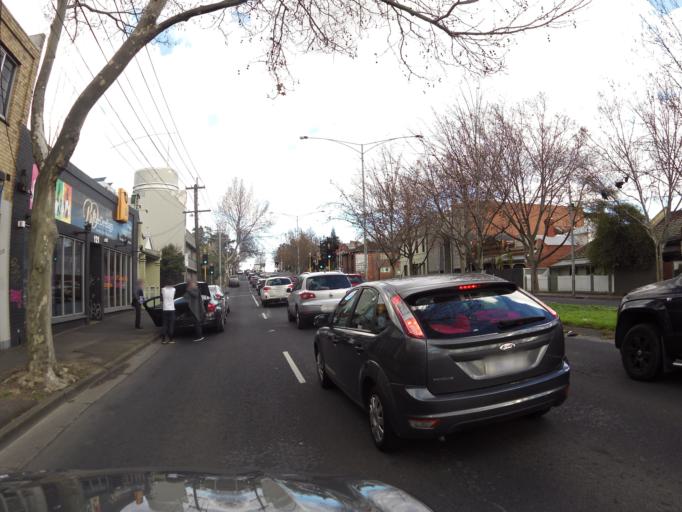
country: AU
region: Victoria
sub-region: Melbourne
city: East Melbourne
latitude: -37.8139
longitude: 144.9907
